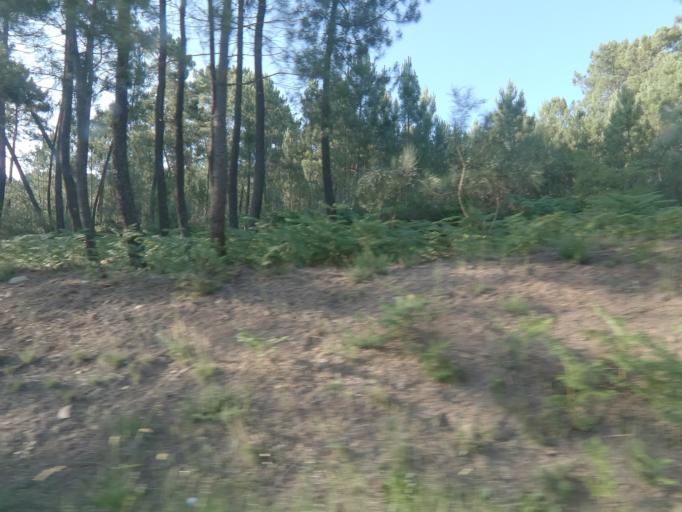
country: PT
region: Vila Real
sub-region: Vila Real
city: Vila Real
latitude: 41.2771
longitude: -7.6784
